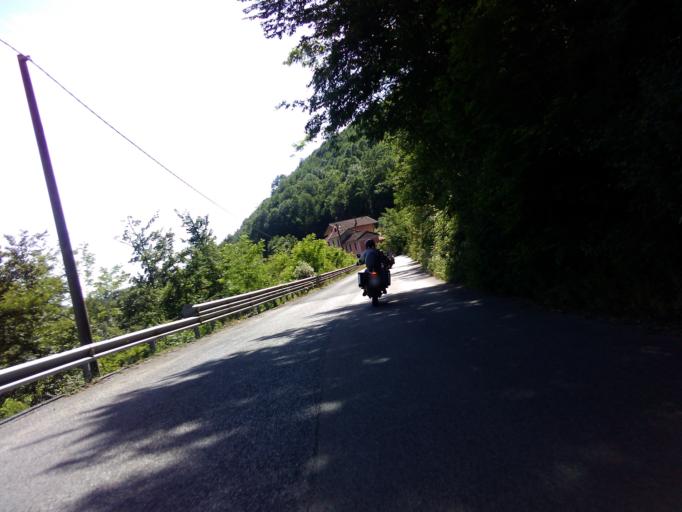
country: IT
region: Tuscany
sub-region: Provincia di Massa-Carrara
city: Licciana Nardi
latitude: 44.2786
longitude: 10.0585
